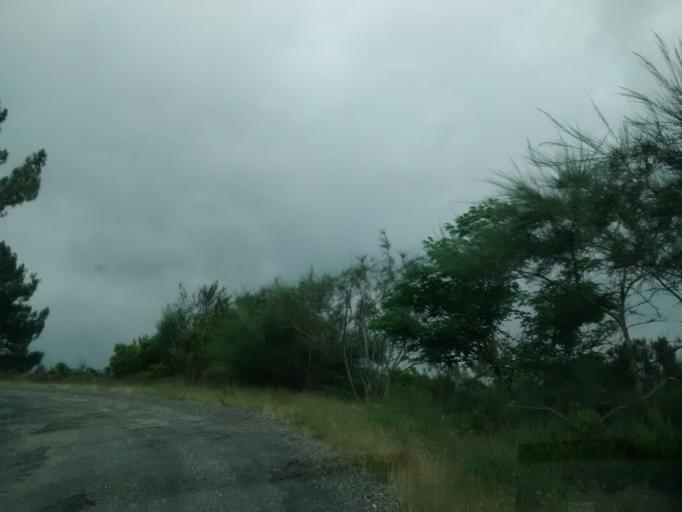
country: ES
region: Galicia
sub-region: Provincia de Ourense
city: Castro Caldelas
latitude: 42.4183
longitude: -7.3886
